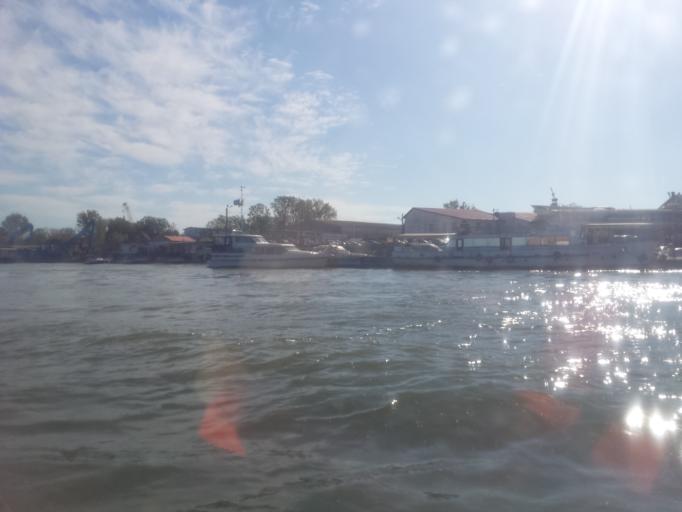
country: RO
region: Tulcea
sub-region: Municipiul Tulcea
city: Tulcea
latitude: 45.1841
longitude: 28.8065
